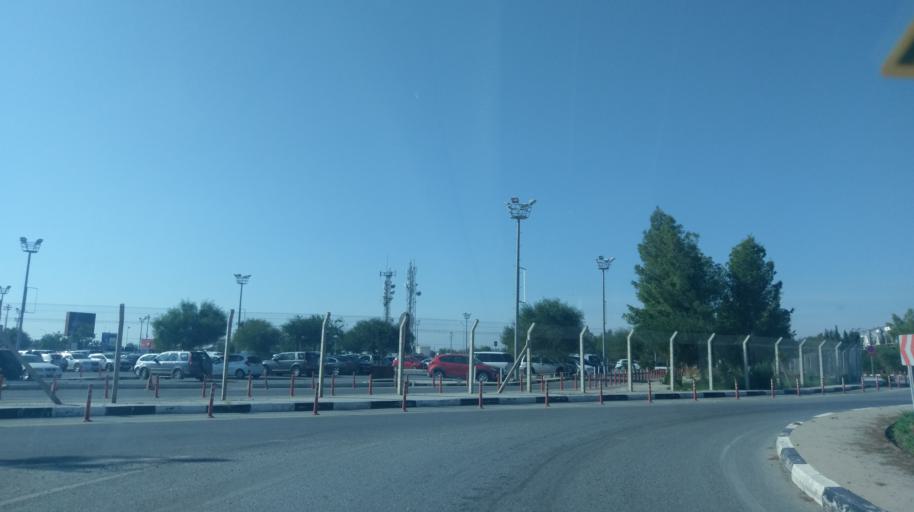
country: CY
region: Lefkosia
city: Geri
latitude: 35.1593
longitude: 33.5046
